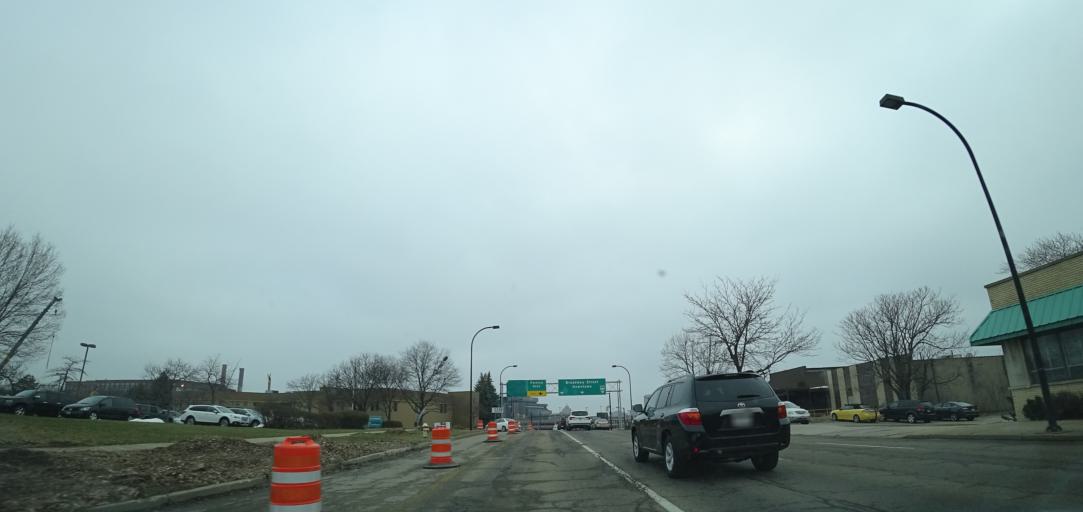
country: US
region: Ohio
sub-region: Summit County
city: Akron
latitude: 41.0675
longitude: -81.5244
